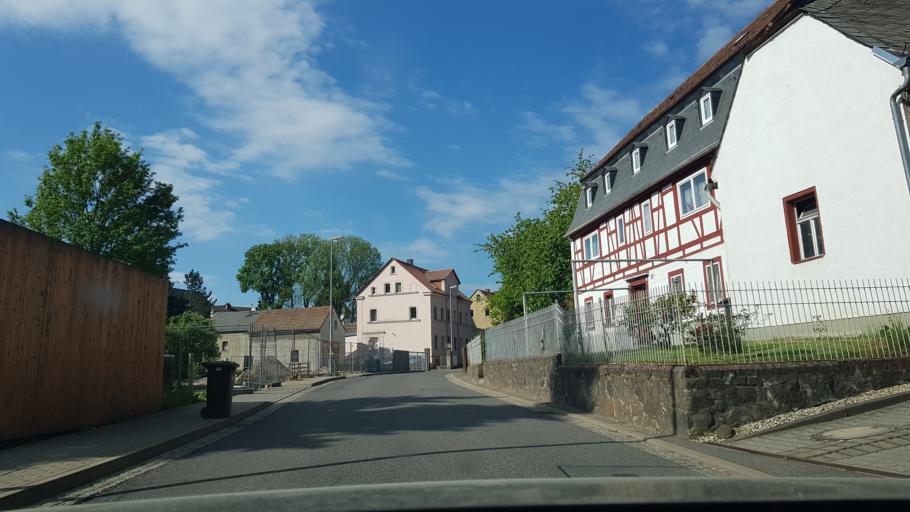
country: DE
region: Saxony
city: Wittgensdorf
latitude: 50.8879
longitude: 12.8792
